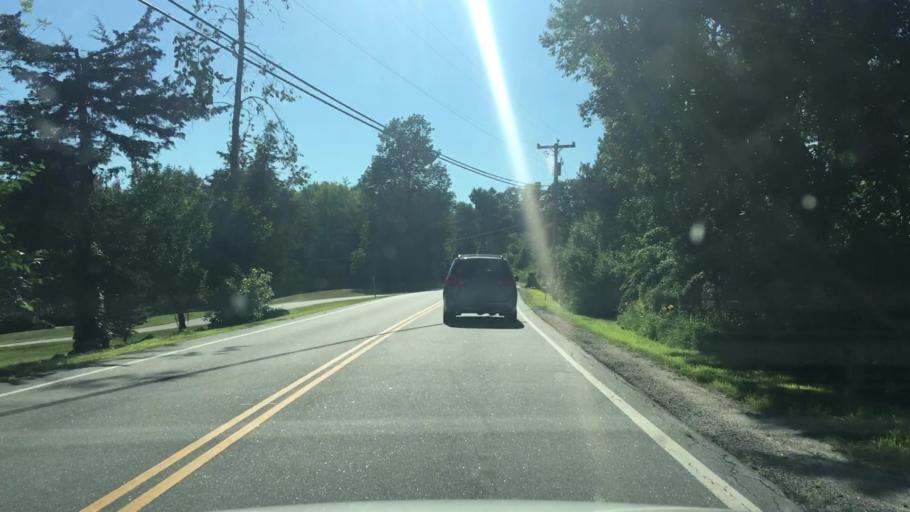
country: US
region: New Hampshire
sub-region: Rockingham County
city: Brentwood
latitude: 42.9915
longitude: -71.0280
